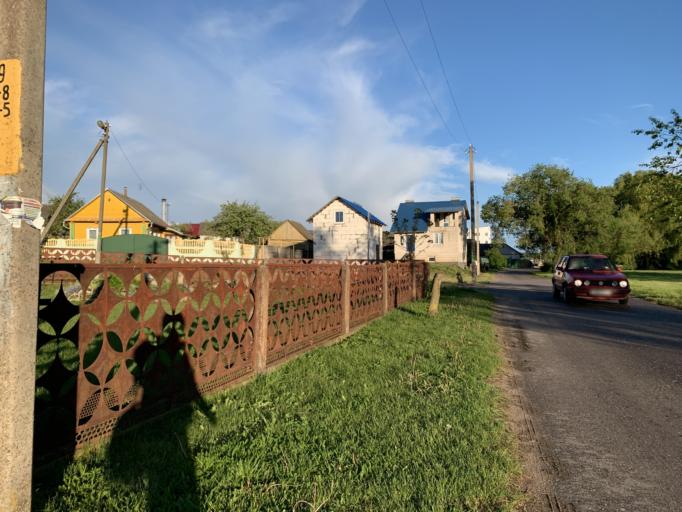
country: BY
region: Minsk
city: Nyasvizh
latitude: 53.2120
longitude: 26.6923
